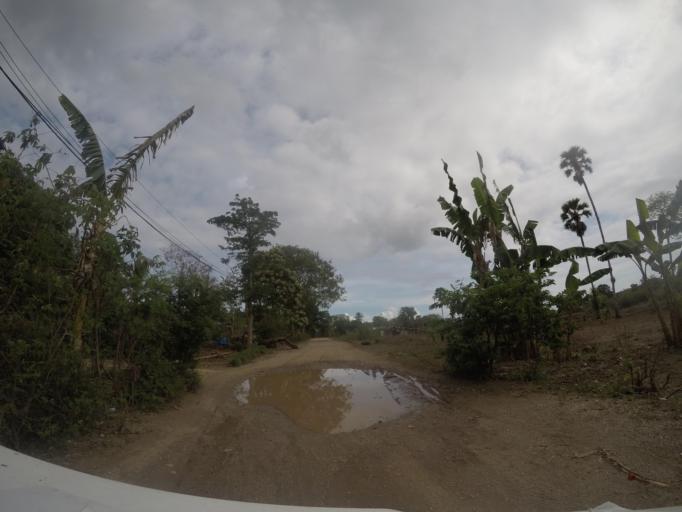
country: TL
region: Baucau
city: Baucau
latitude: -8.4741
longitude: 126.4539
